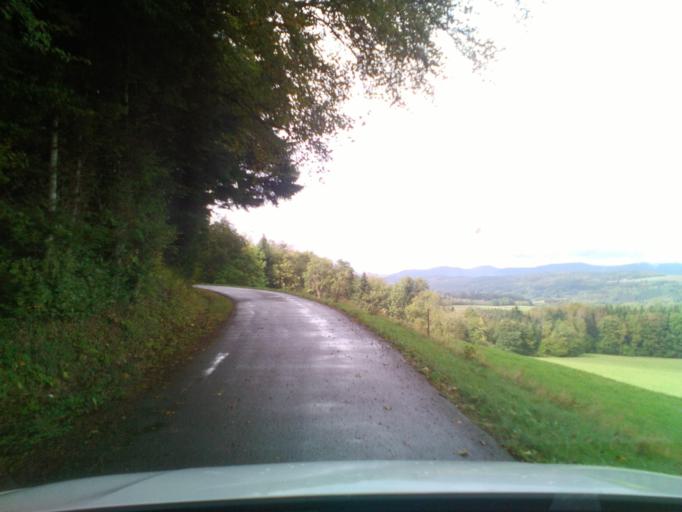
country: FR
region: Lorraine
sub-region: Departement des Vosges
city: Sainte-Marguerite
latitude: 48.3207
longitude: 6.9902
